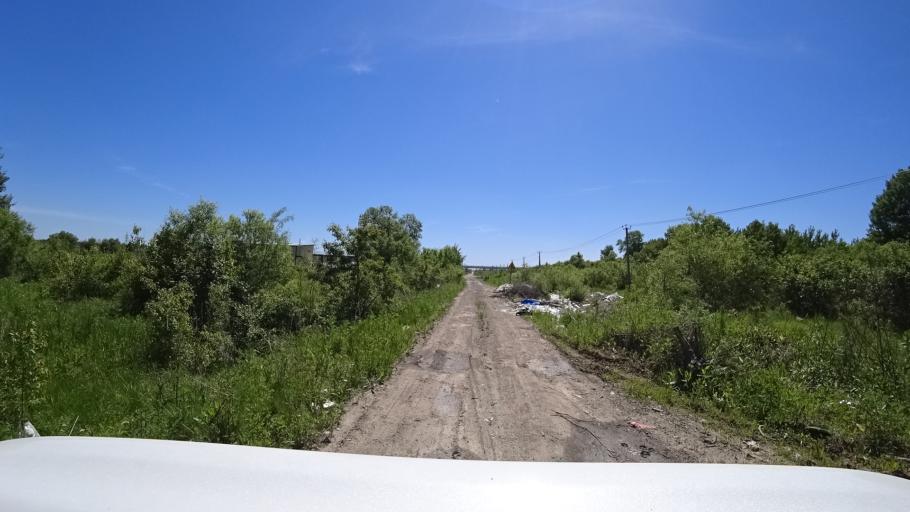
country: RU
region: Khabarovsk Krai
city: Topolevo
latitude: 48.4857
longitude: 135.1763
